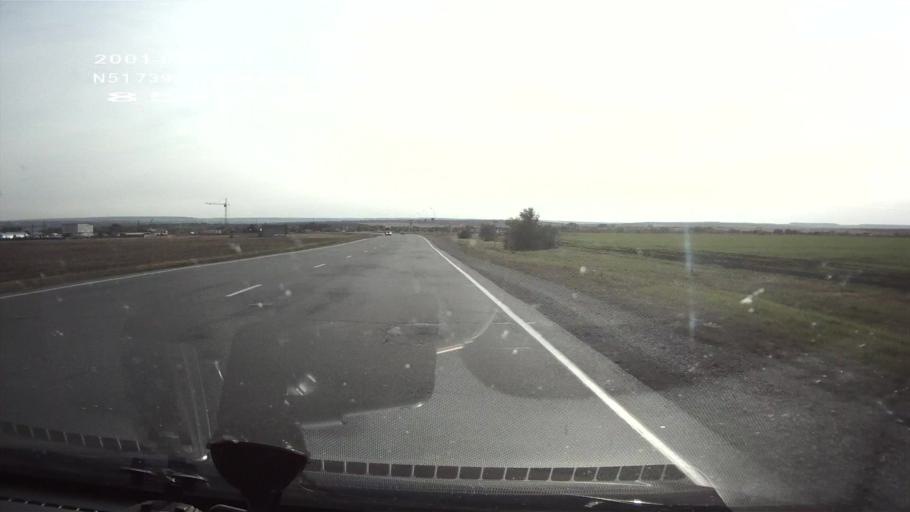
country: RU
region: Saratov
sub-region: Saratovskiy Rayon
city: Saratov
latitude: 51.7393
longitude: 46.0419
